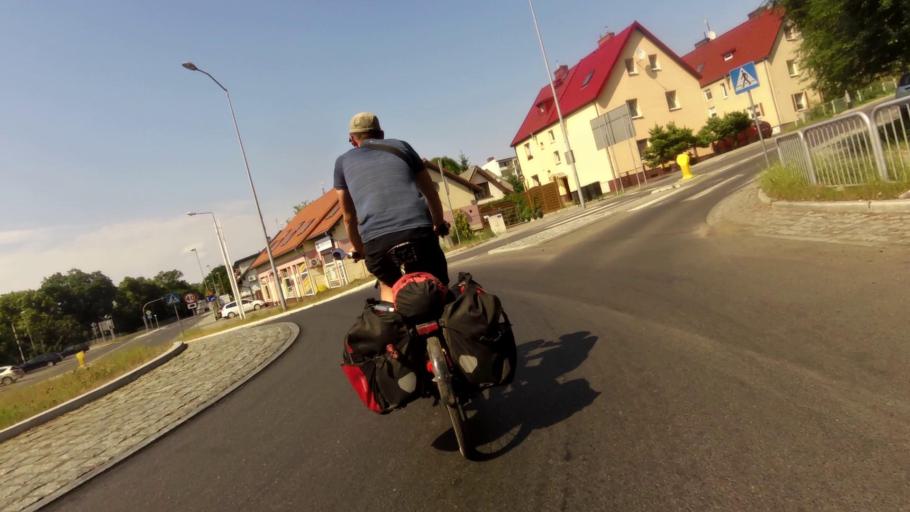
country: PL
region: West Pomeranian Voivodeship
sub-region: Powiat gryfinski
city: Gryfino
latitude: 53.2503
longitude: 14.4947
